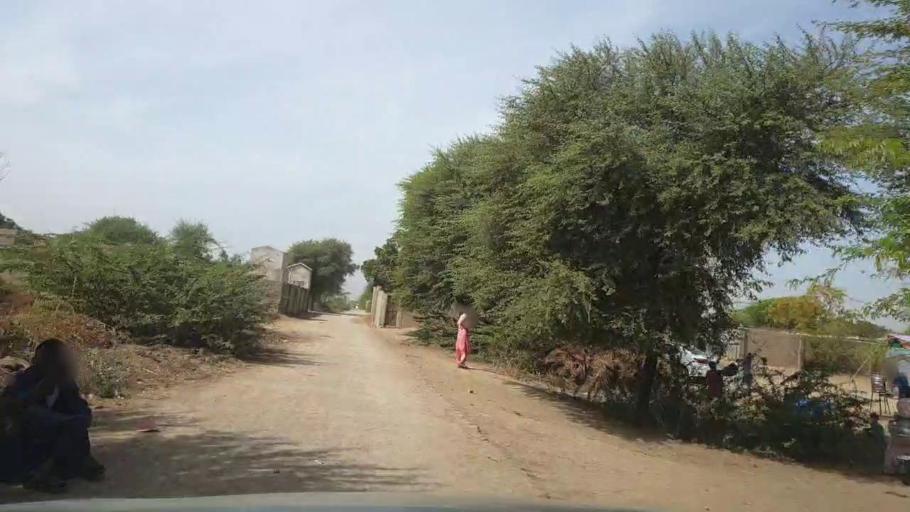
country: PK
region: Sindh
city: Nabisar
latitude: 25.1190
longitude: 69.6000
